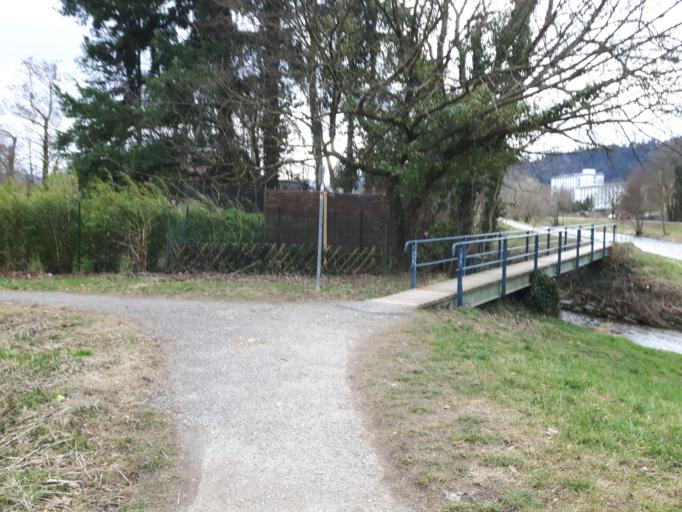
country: DE
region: Baden-Wuerttemberg
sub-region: Freiburg Region
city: Freiburg
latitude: 47.9870
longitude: 7.8997
